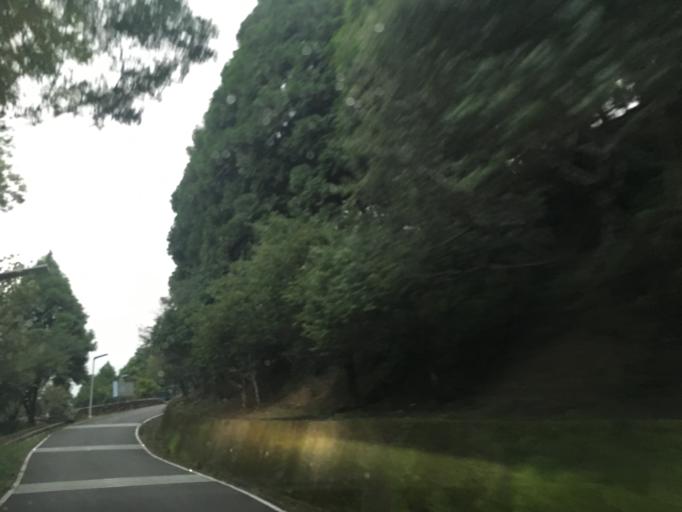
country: TW
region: Taiwan
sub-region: Nantou
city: Puli
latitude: 23.9045
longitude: 120.9066
